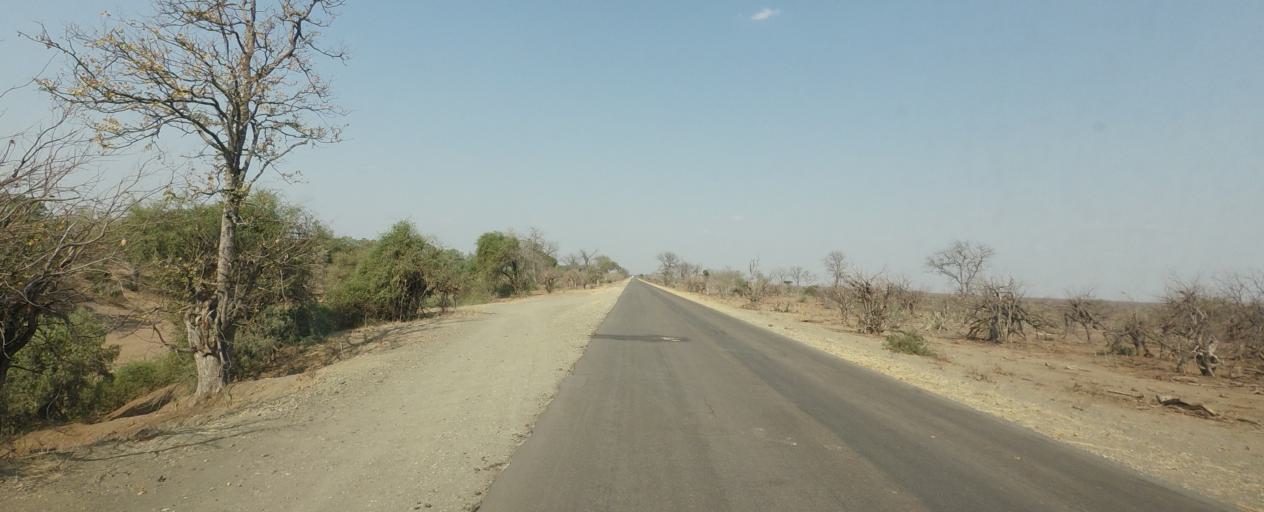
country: ZA
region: Limpopo
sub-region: Mopani District Municipality
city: Giyani
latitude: -23.0969
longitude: 31.3957
